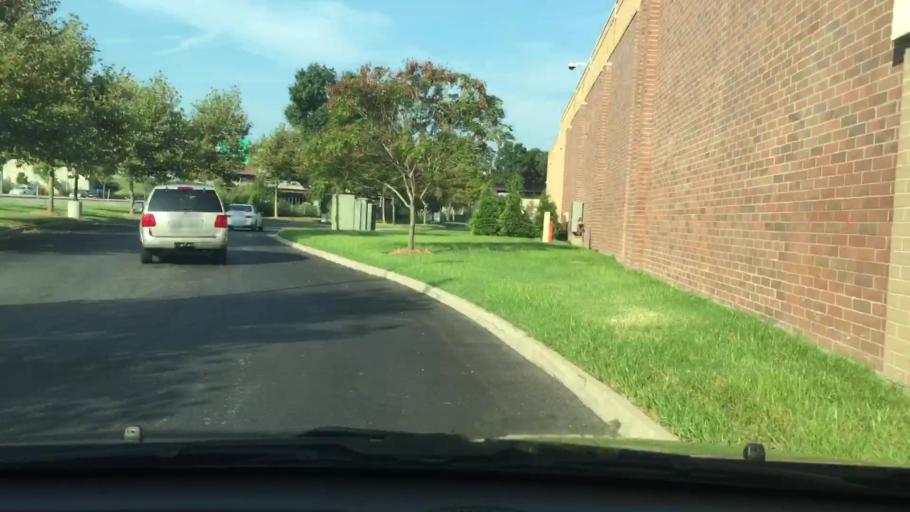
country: US
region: Virginia
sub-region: City of Hampton
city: Hampton
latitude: 37.0417
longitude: -76.3909
